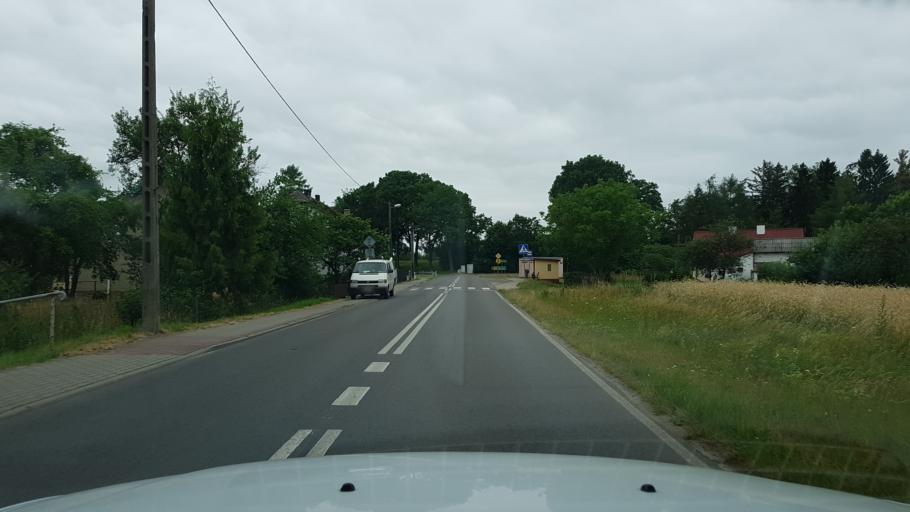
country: PL
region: West Pomeranian Voivodeship
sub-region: Powiat gryficki
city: Brojce
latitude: 53.9559
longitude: 15.3685
